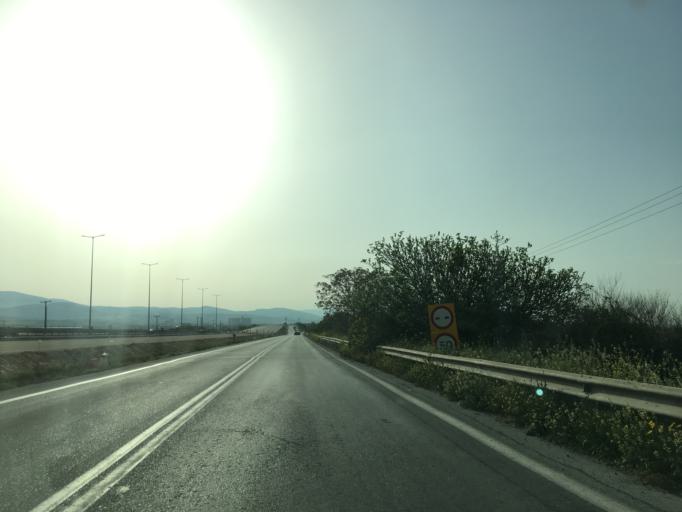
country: GR
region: Thessaly
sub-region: Nomos Magnisias
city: Velestino
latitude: 39.3854
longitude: 22.7983
